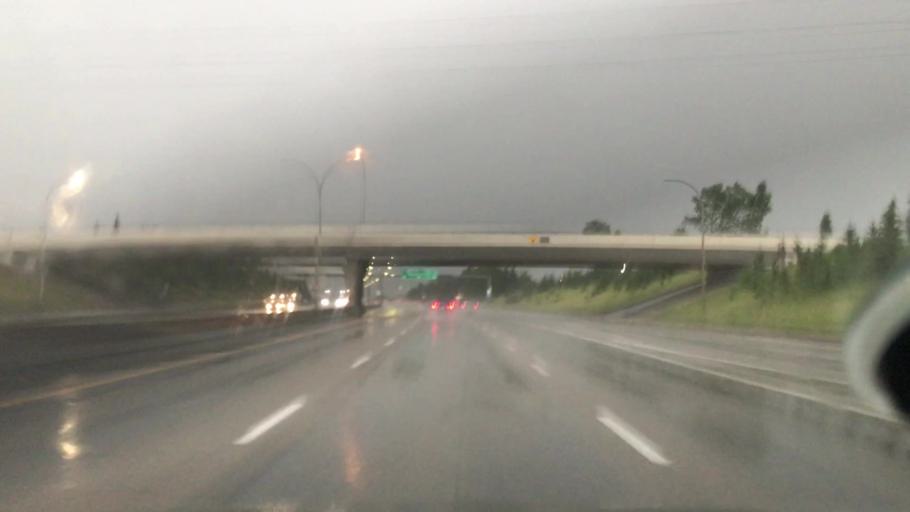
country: CA
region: Alberta
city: Edmonton
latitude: 53.4807
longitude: -113.4806
